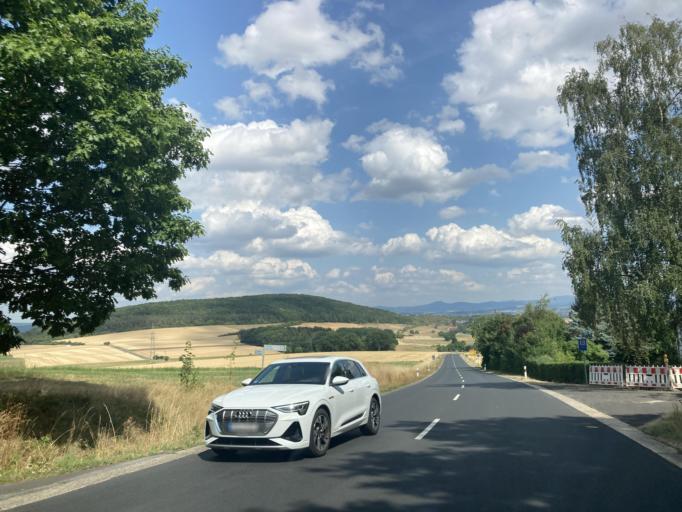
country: DE
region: Hesse
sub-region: Regierungsbezirk Kassel
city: Grossenluder
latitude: 50.5417
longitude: 9.5798
